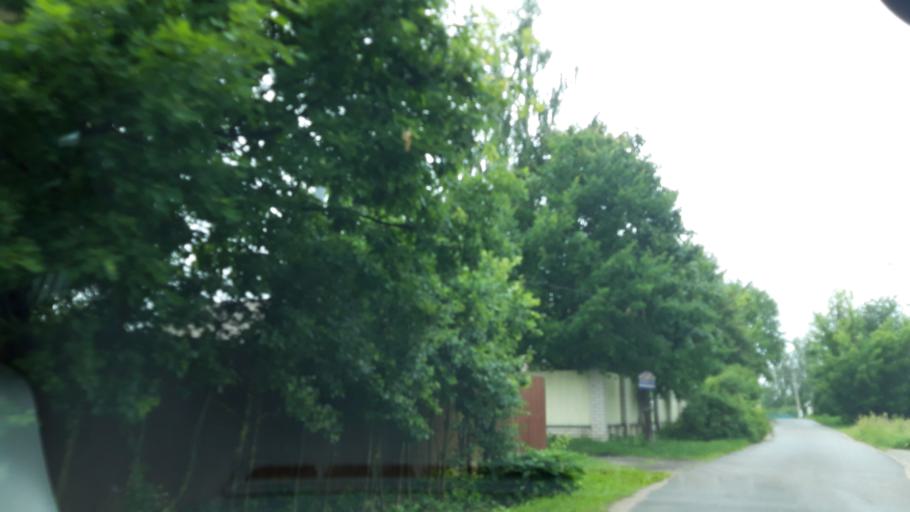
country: RU
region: Tverskaya
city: Konakovo
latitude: 56.6629
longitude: 36.6616
